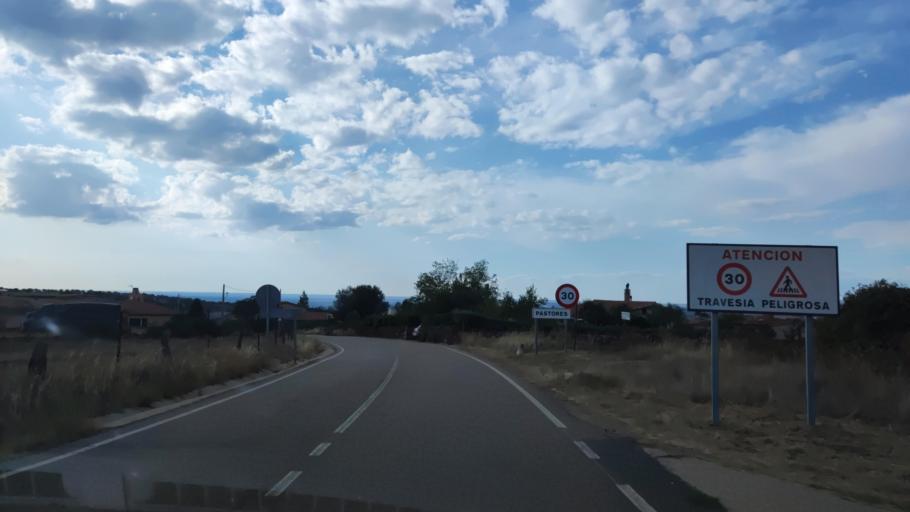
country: ES
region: Castille and Leon
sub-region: Provincia de Salamanca
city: Pastores
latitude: 40.5142
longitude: -6.5070
